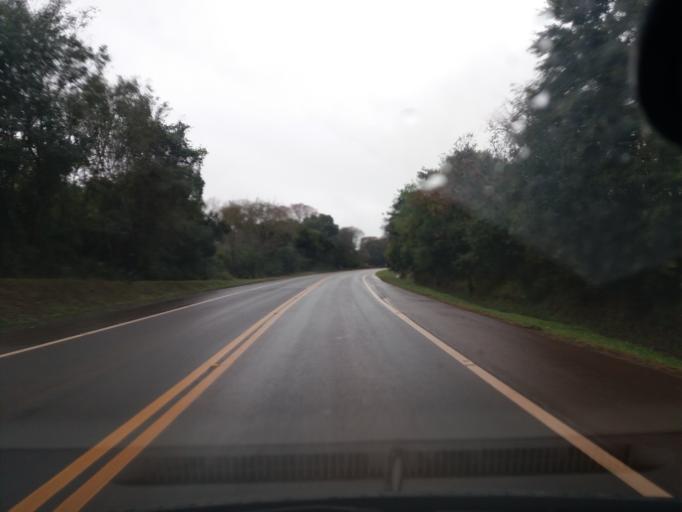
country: BR
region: Parana
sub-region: Campo Mourao
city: Campo Mourao
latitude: -24.3199
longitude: -52.6405
